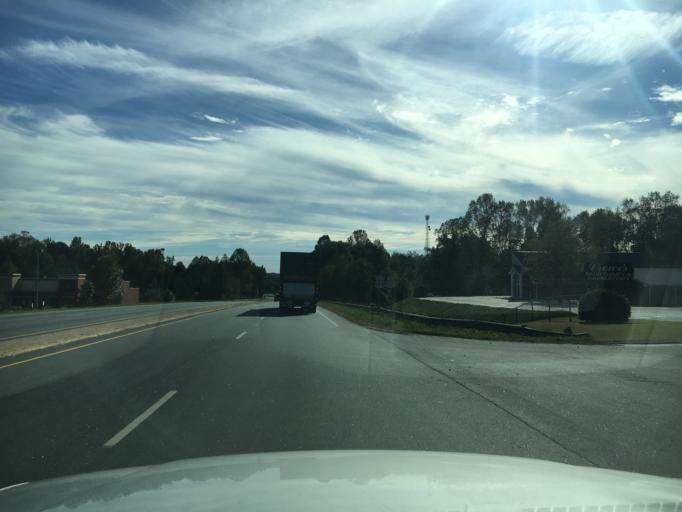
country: US
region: North Carolina
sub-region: Rutherford County
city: Spindale
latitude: 35.3627
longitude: -81.9420
